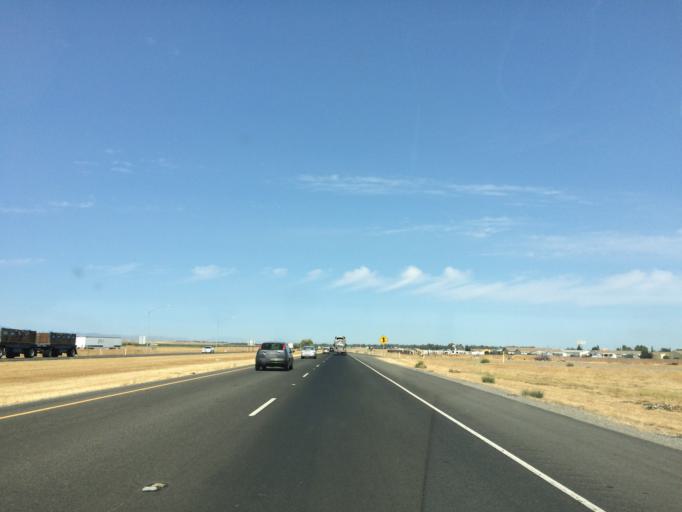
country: US
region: California
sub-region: Yolo County
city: Dunnigan
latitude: 38.8618
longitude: -121.9542
